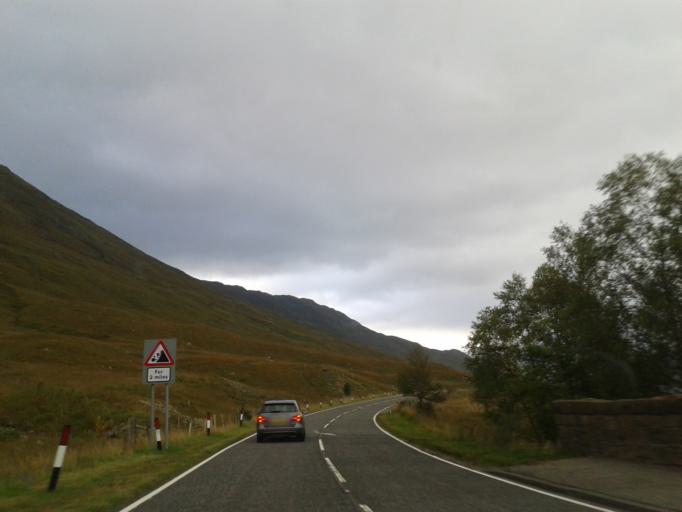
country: GB
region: Scotland
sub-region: Highland
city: Fort William
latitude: 57.1600
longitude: -5.1594
